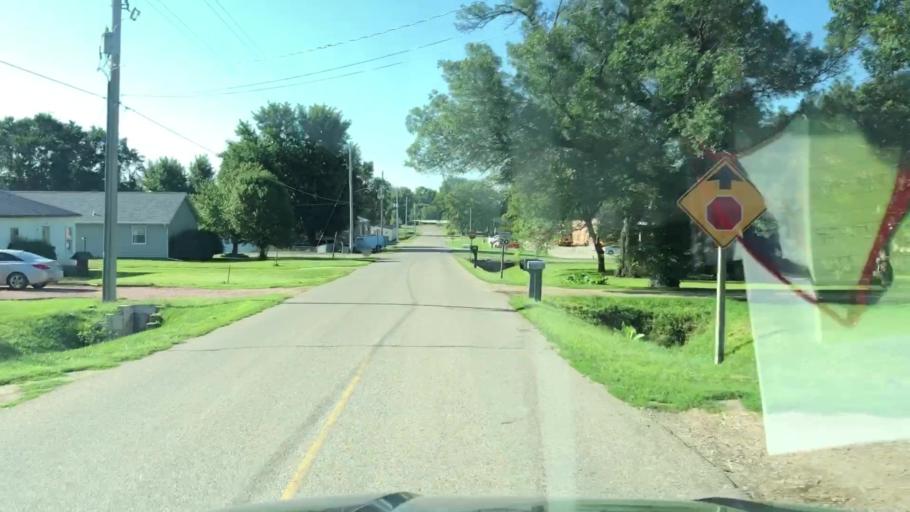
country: US
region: Iowa
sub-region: Woodbury County
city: Sergeant Bluff
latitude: 42.4113
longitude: -96.2138
